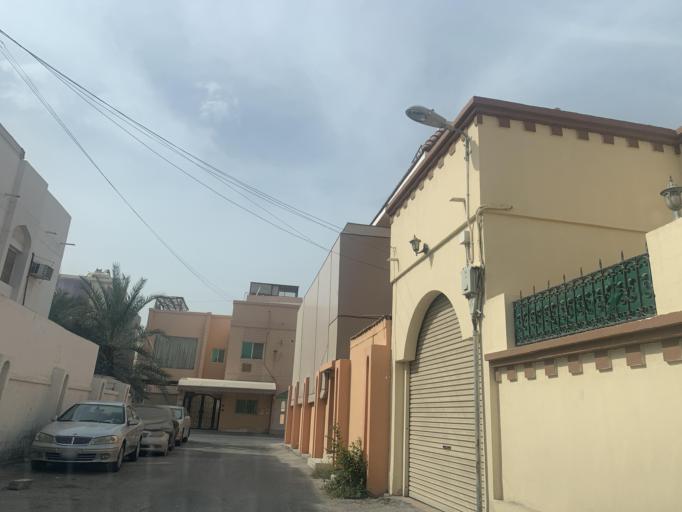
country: BH
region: Northern
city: Ar Rifa'
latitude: 26.1323
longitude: 50.5577
